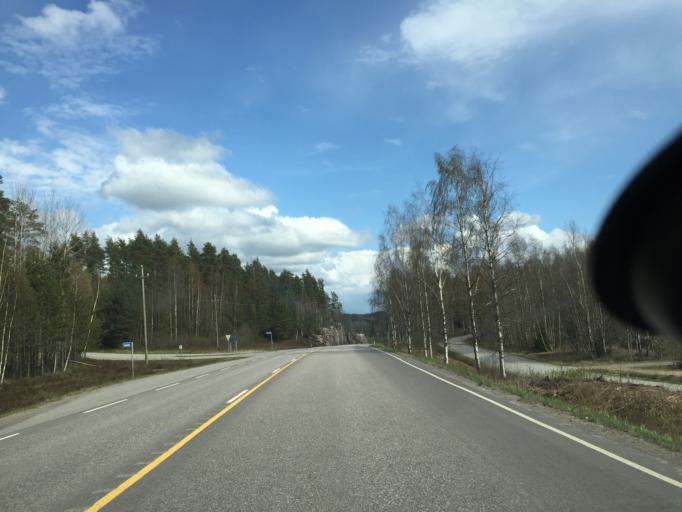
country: FI
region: Uusimaa
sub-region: Raaseporin
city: Ekenaes
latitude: 60.0604
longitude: 23.3157
